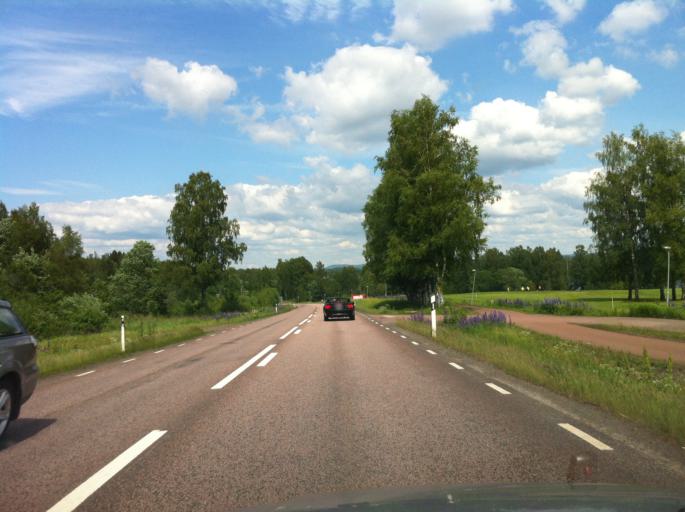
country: SE
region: Vaermland
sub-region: Sunne Kommun
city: Sunne
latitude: 59.8138
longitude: 13.1278
